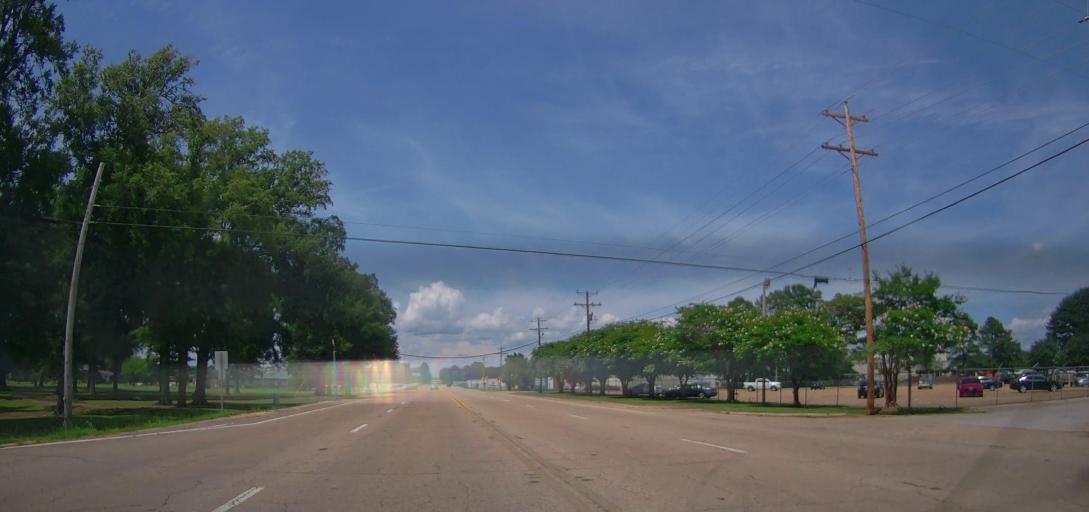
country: US
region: Mississippi
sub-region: Lee County
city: Verona
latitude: 34.1624
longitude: -88.7195
